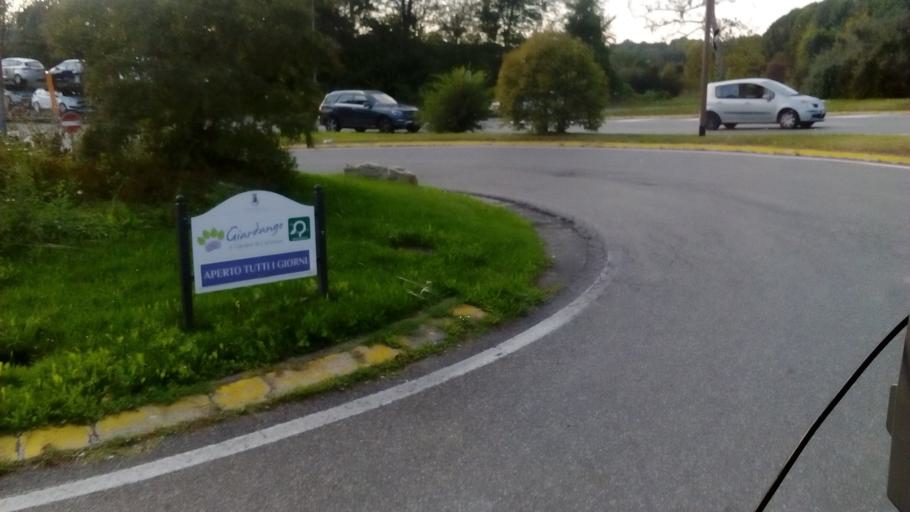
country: IT
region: Lombardy
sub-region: Provincia di Como
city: Novedrate
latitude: 45.6949
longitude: 9.1170
